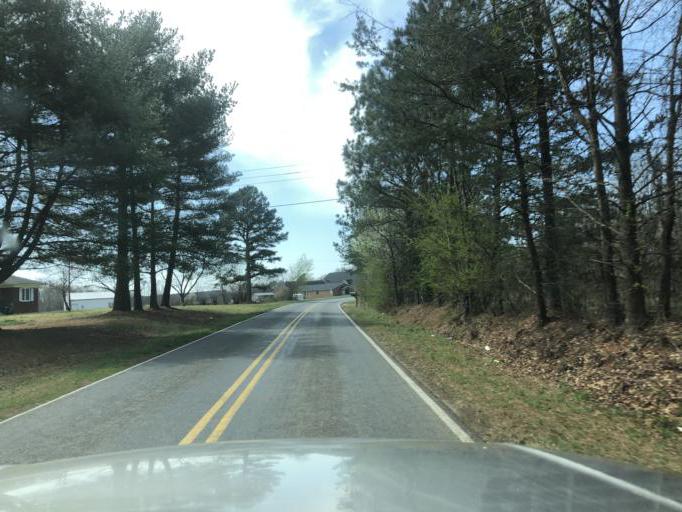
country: US
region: North Carolina
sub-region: Cleveland County
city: Shelby
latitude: 35.2473
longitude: -81.5349
